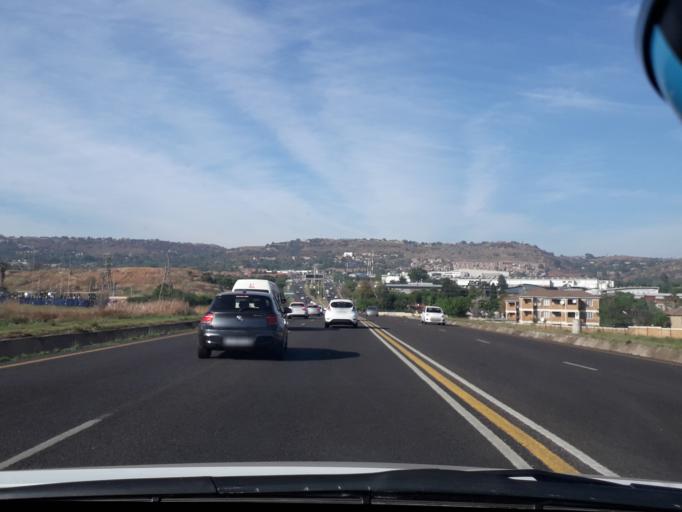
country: ZA
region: Gauteng
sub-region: City of Johannesburg Metropolitan Municipality
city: Roodepoort
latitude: -26.1199
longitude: 27.9135
